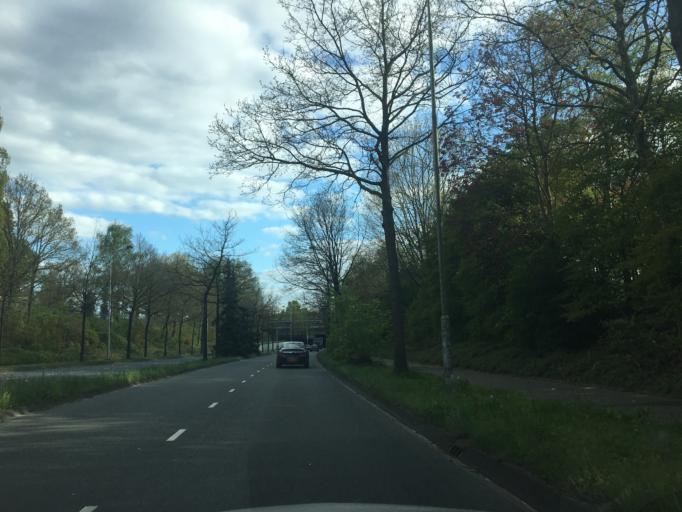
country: NL
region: Gelderland
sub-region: Gemeente Ede
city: Ede
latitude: 52.0296
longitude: 5.6730
